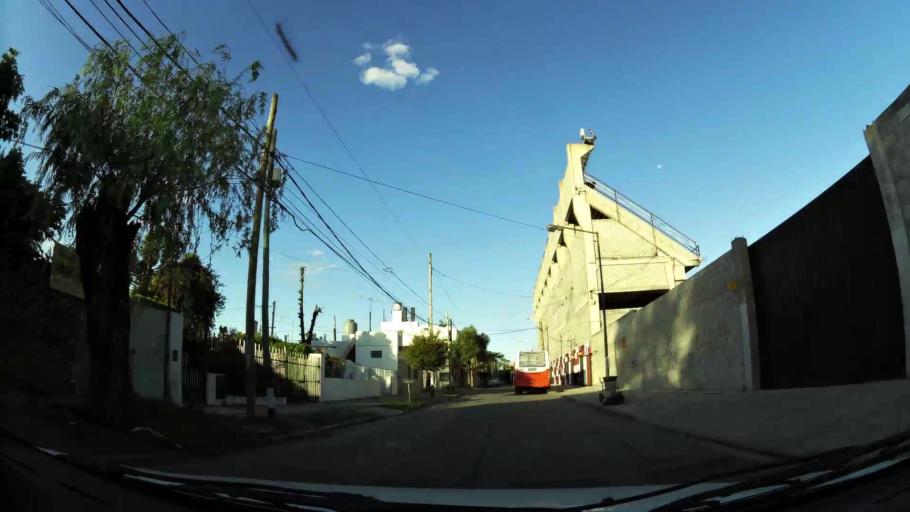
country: AR
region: Buenos Aires
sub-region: Partido de General San Martin
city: General San Martin
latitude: -34.5674
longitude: -58.5292
